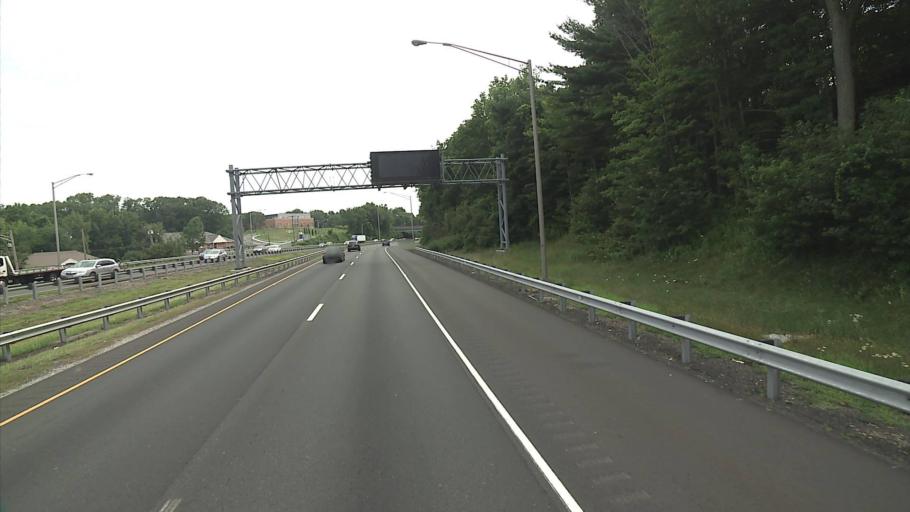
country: US
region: Connecticut
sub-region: New Haven County
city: Waterbury
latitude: 41.5463
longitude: -73.0707
